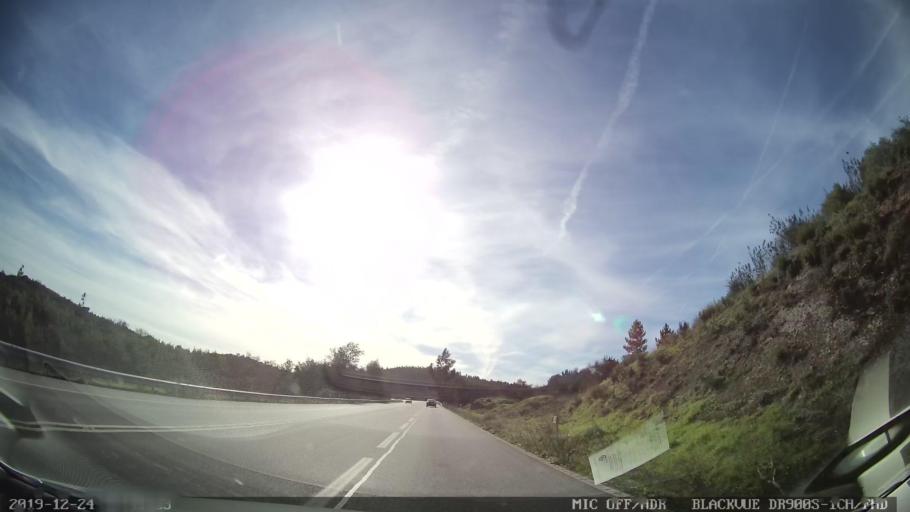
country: PT
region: Portalegre
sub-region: Nisa
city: Nisa
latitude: 39.5091
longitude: -7.7706
